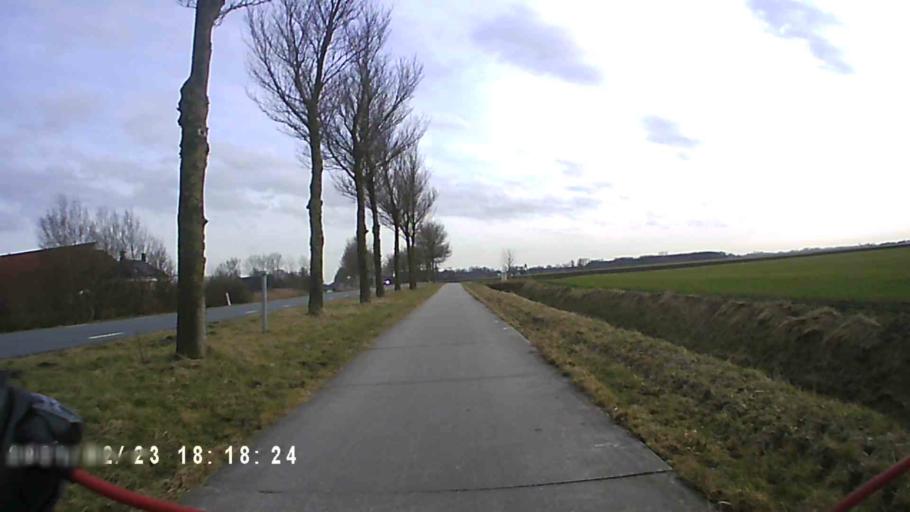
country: NL
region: Groningen
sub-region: Gemeente Bedum
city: Bedum
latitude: 53.3752
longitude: 6.6288
